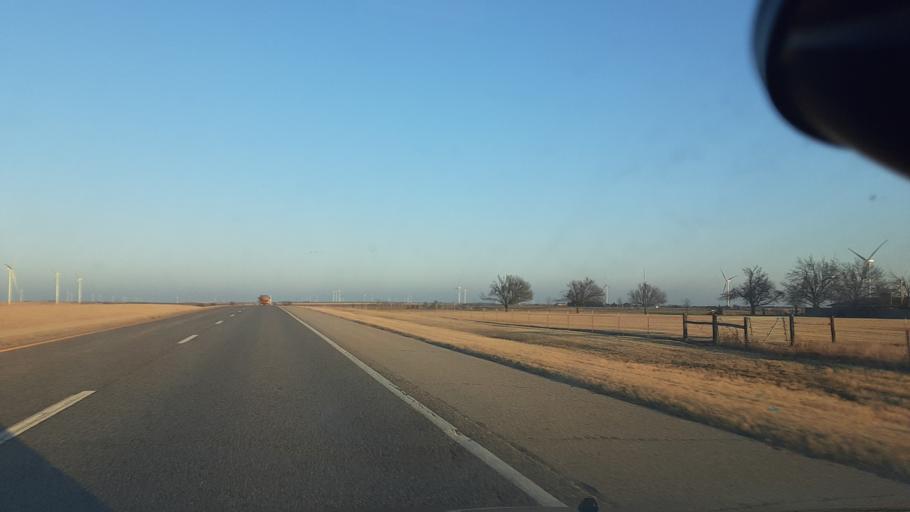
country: US
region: Oklahoma
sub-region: Noble County
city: Perry
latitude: 36.3974
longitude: -97.5124
